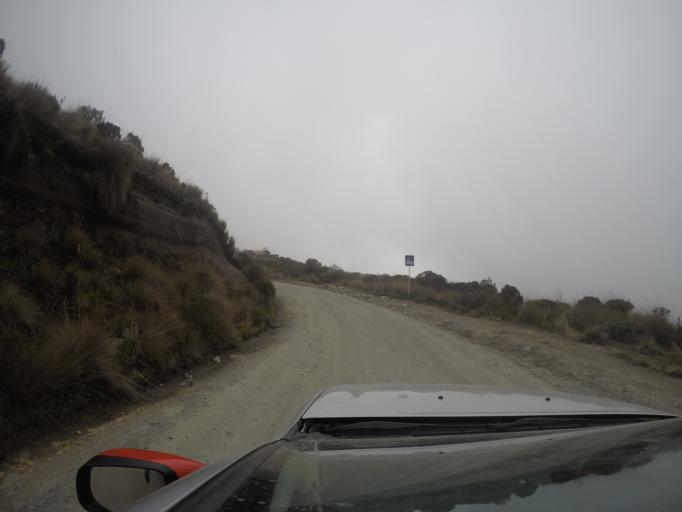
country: CO
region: Tolima
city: Murillo
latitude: 4.9338
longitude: -75.3491
